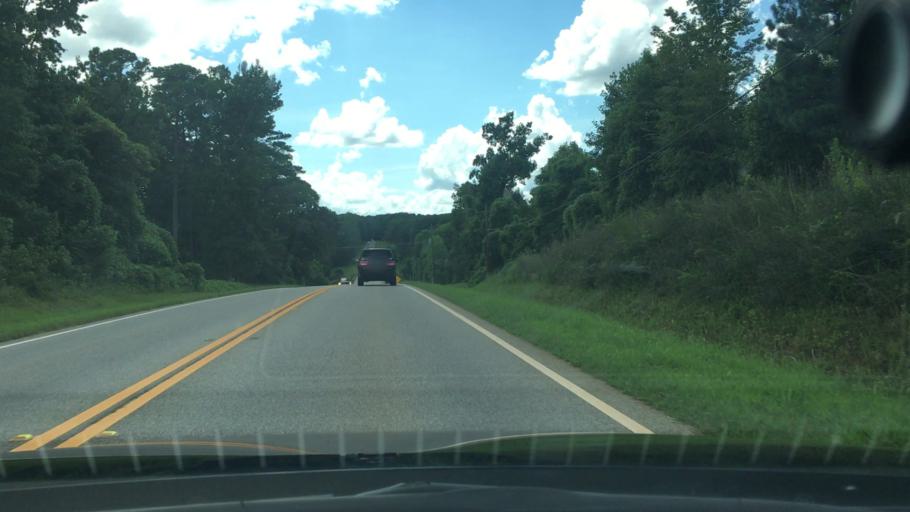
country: US
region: Georgia
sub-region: Putnam County
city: Eatonton
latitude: 33.3152
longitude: -83.4322
